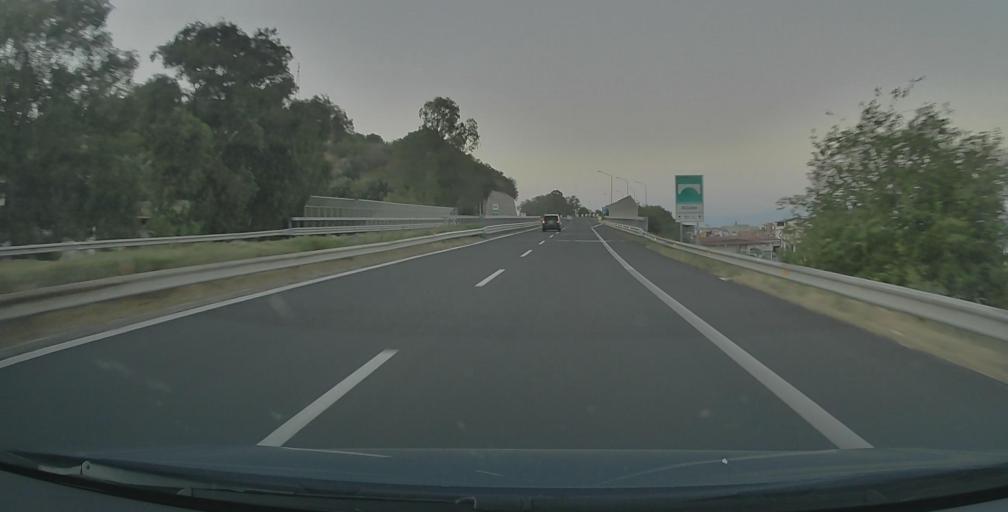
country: IT
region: Sicily
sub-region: Messina
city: Roccalumera
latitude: 37.9827
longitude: 15.3998
